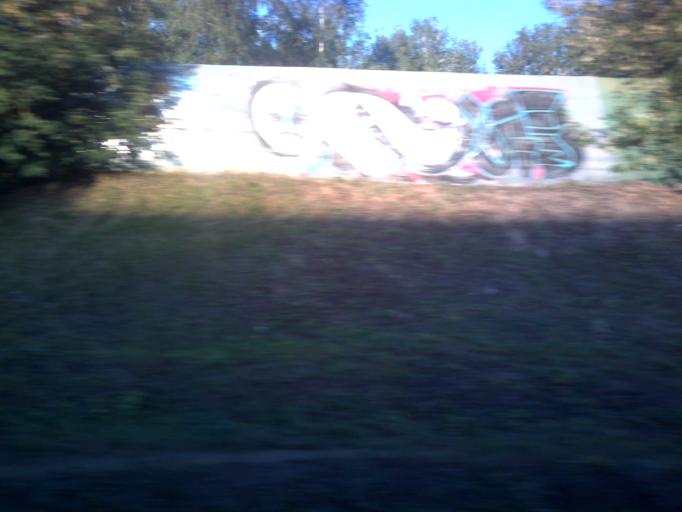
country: RU
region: Moscow
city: Kotlovka
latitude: 55.6769
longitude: 37.6220
